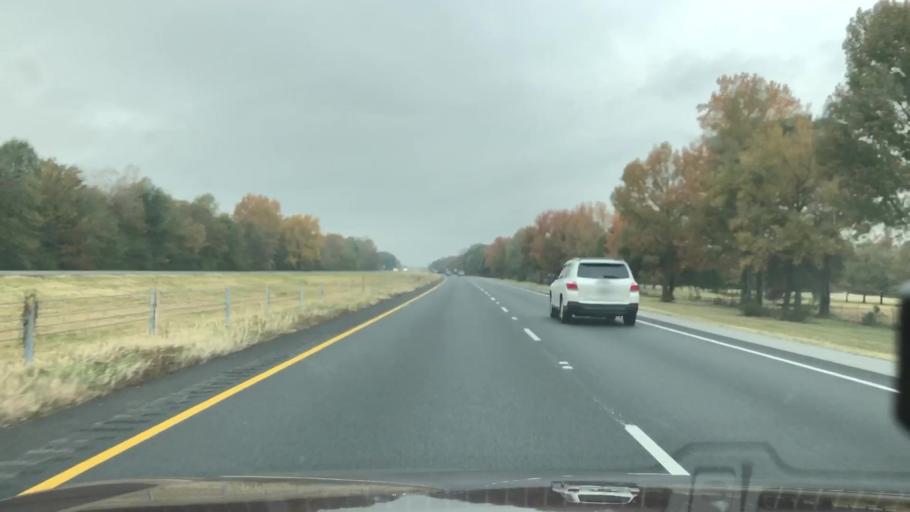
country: US
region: Louisiana
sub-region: Richland Parish
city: Rayville
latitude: 32.4668
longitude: -91.8028
